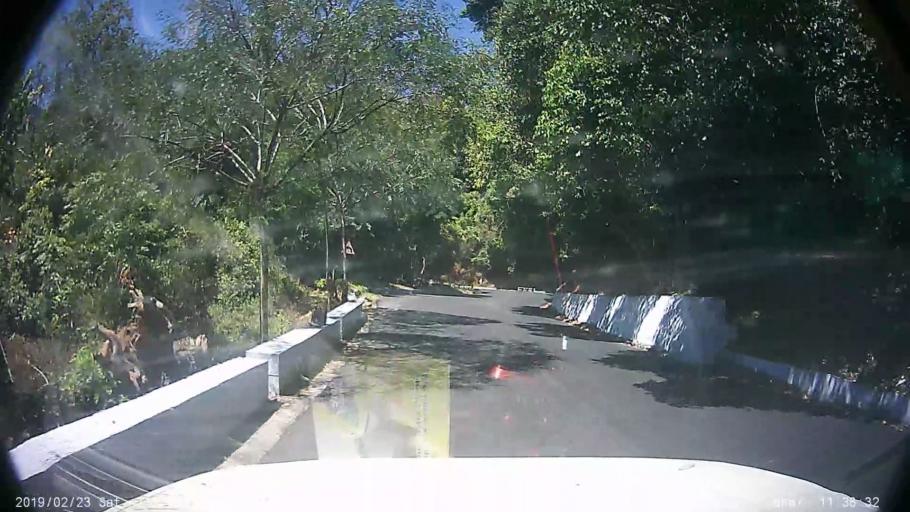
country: IN
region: Tamil Nadu
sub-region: Nilgiri
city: Wellington
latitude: 11.3405
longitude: 76.8447
